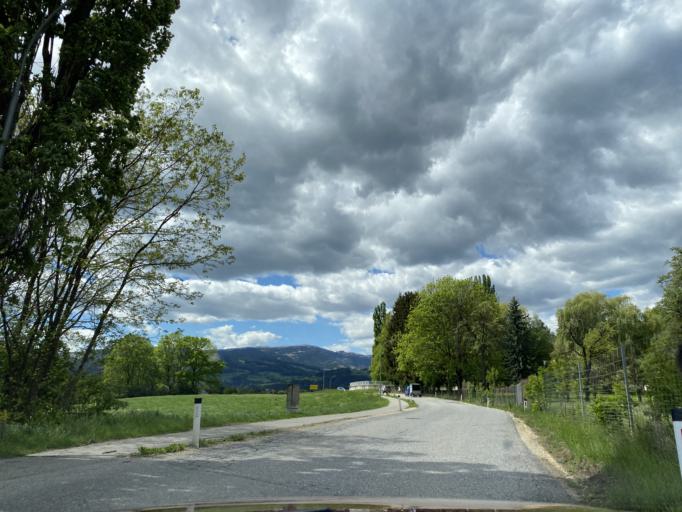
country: AT
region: Carinthia
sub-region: Politischer Bezirk Wolfsberg
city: Wolfsberg
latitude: 46.8433
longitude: 14.8365
